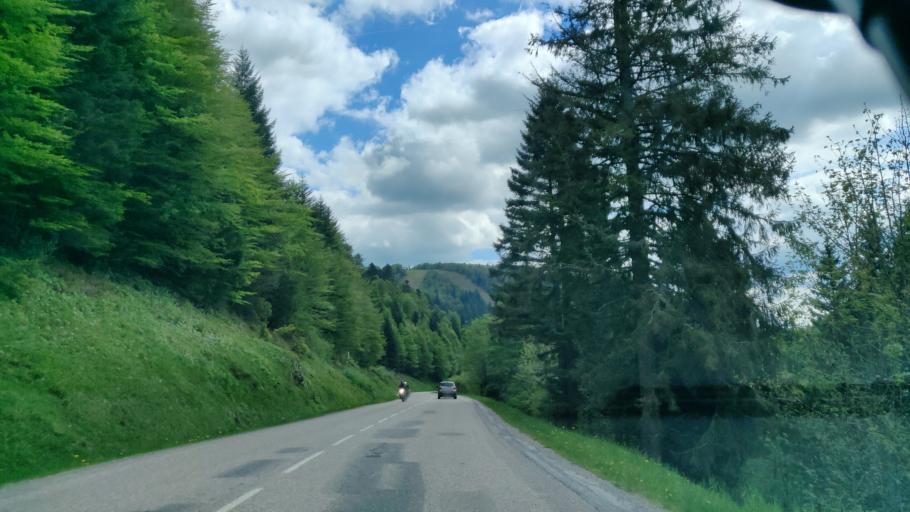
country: FR
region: Lorraine
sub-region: Departement des Vosges
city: Xonrupt-Longemer
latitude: 48.0452
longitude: 6.9761
